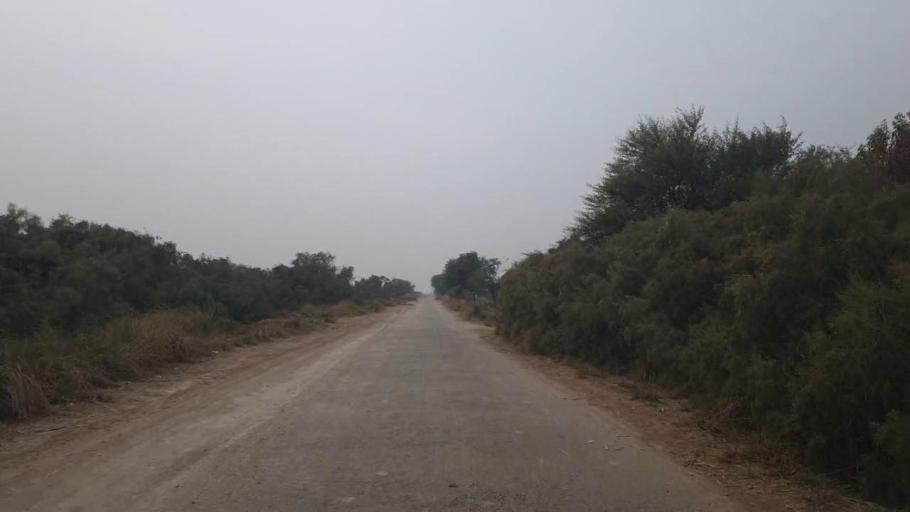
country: PK
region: Sindh
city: Shahdadpur
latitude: 25.8667
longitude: 68.6318
